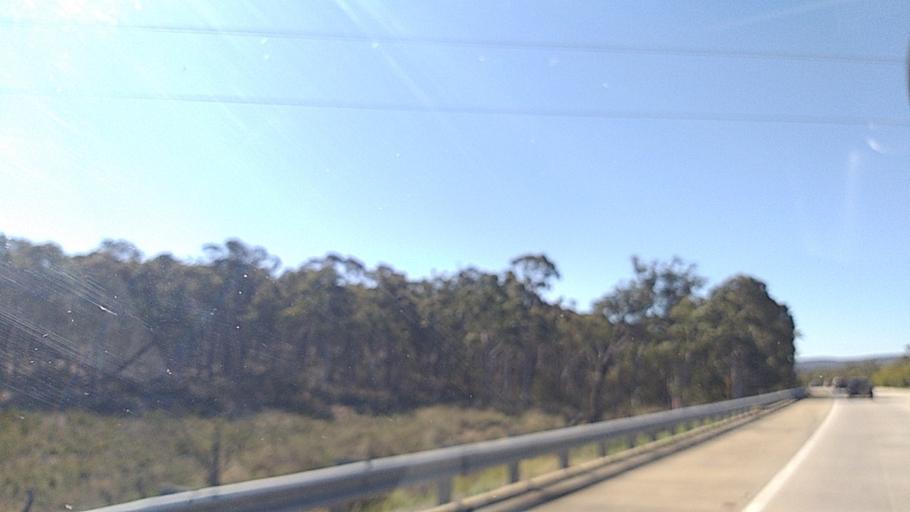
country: AU
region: New South Wales
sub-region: Yass Valley
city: Gundaroo
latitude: -35.1594
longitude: 149.3208
